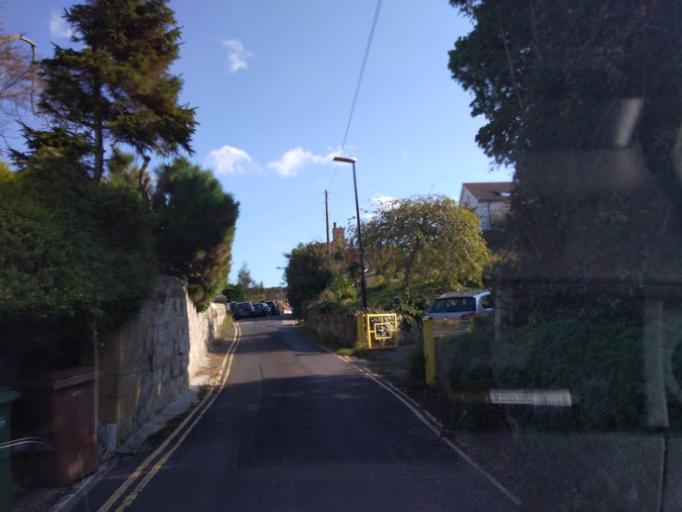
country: GB
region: England
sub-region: East Sussex
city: Hastings
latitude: 50.8620
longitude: 0.6000
